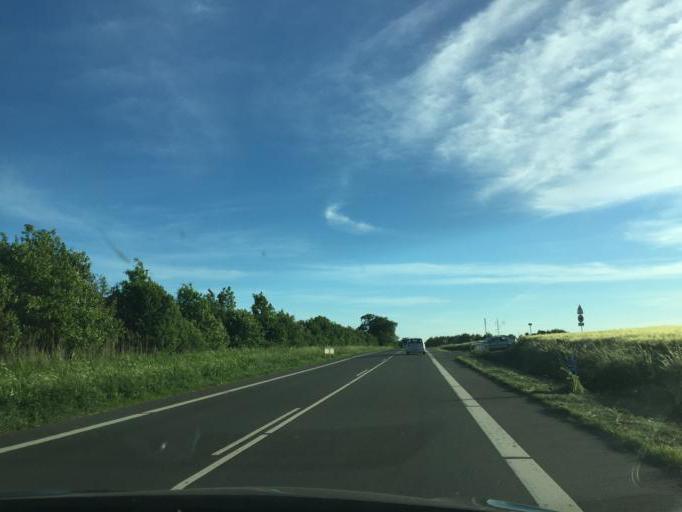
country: DK
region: Zealand
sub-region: Slagelse Kommune
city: Forlev
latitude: 55.3750
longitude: 11.2923
